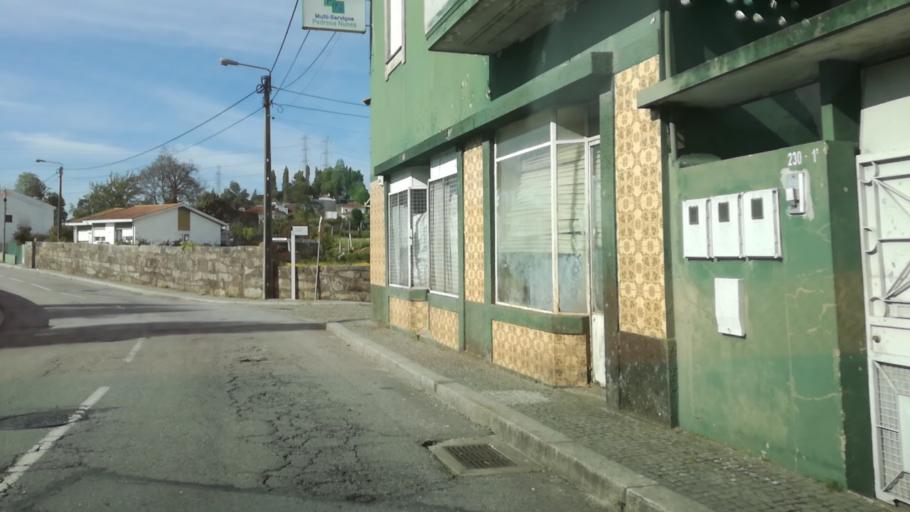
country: PT
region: Porto
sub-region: Maia
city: Nogueira
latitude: 41.2317
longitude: -8.5871
